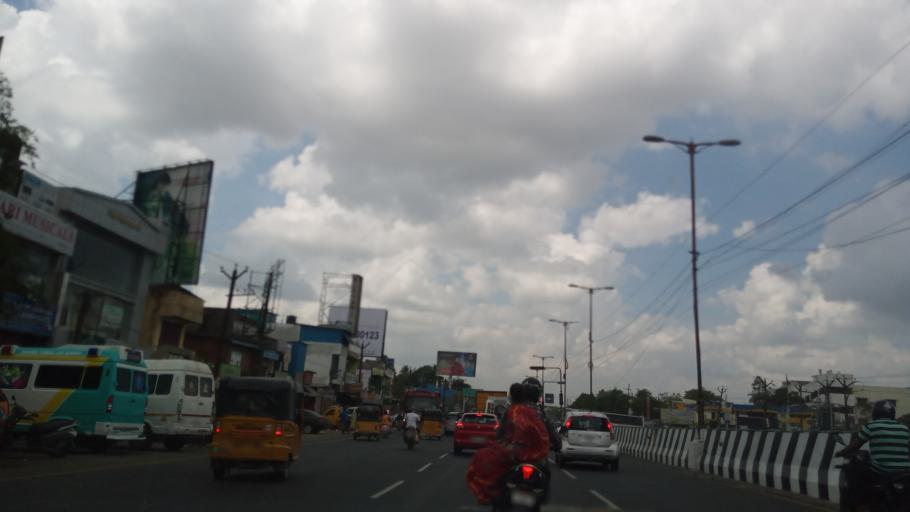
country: IN
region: Tamil Nadu
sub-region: Kancheepuram
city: Pallavaram
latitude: 12.9323
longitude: 80.1237
